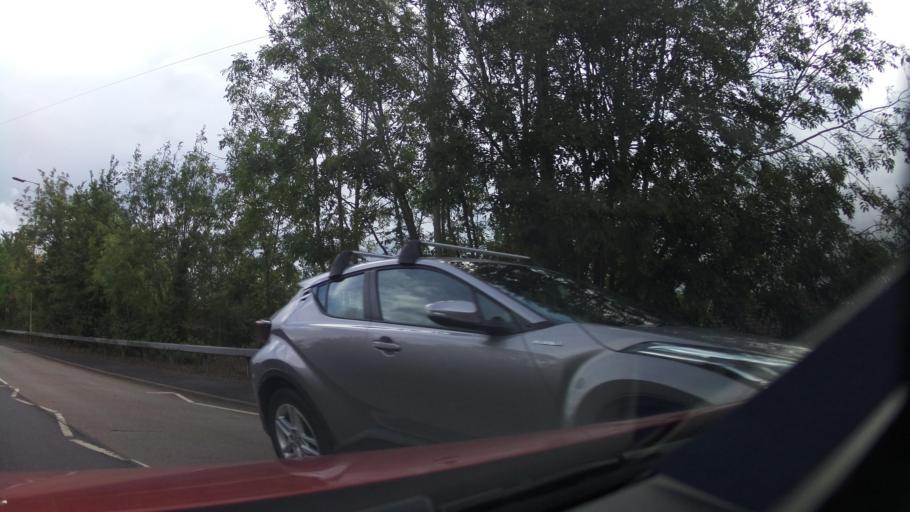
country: GB
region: England
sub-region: Shropshire
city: Bridgnorth
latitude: 52.5304
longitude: -2.4120
